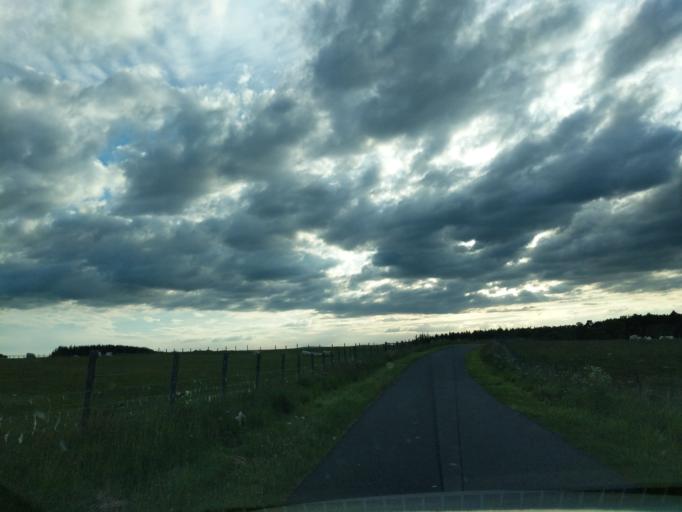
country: GB
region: Scotland
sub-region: Midlothian
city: Penicuik
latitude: 55.7647
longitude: -3.1352
